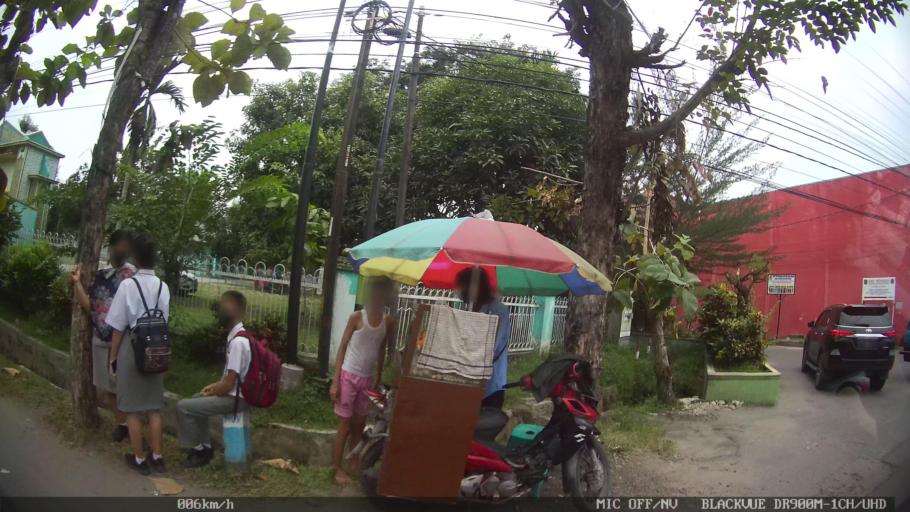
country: ID
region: North Sumatra
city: Medan
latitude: 3.5661
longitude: 98.7230
